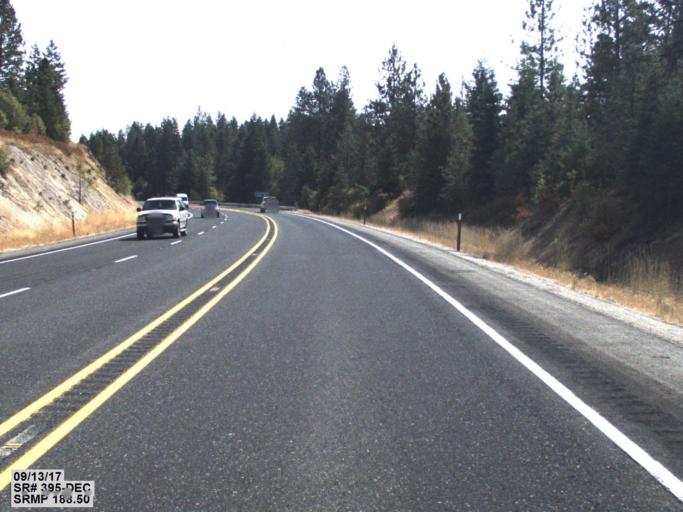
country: US
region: Washington
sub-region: Spokane County
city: Deer Park
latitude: 48.0327
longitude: -117.6040
